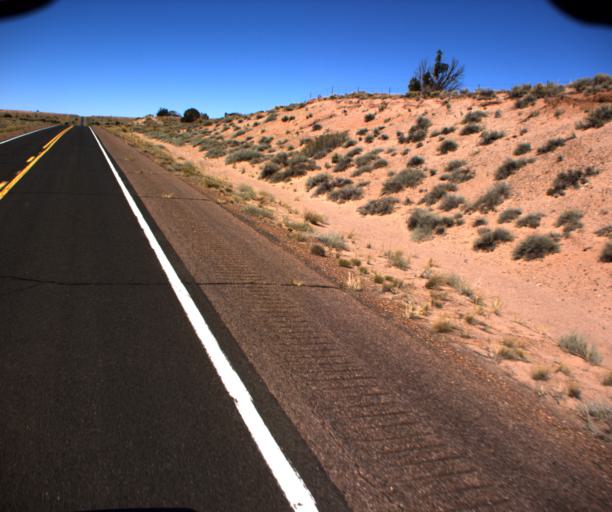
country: US
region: Arizona
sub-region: Navajo County
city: Snowflake
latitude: 34.6734
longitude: -109.7274
